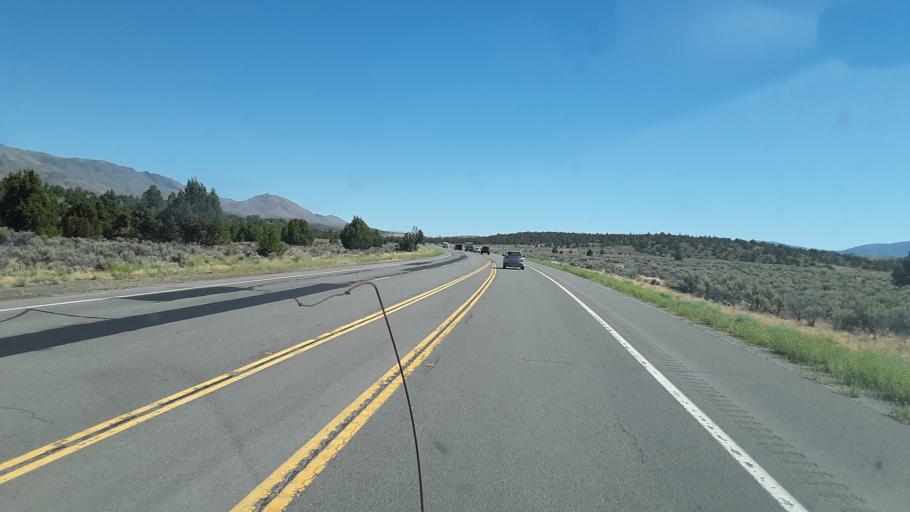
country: US
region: Nevada
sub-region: Washoe County
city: Cold Springs
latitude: 39.8502
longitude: -120.0437
